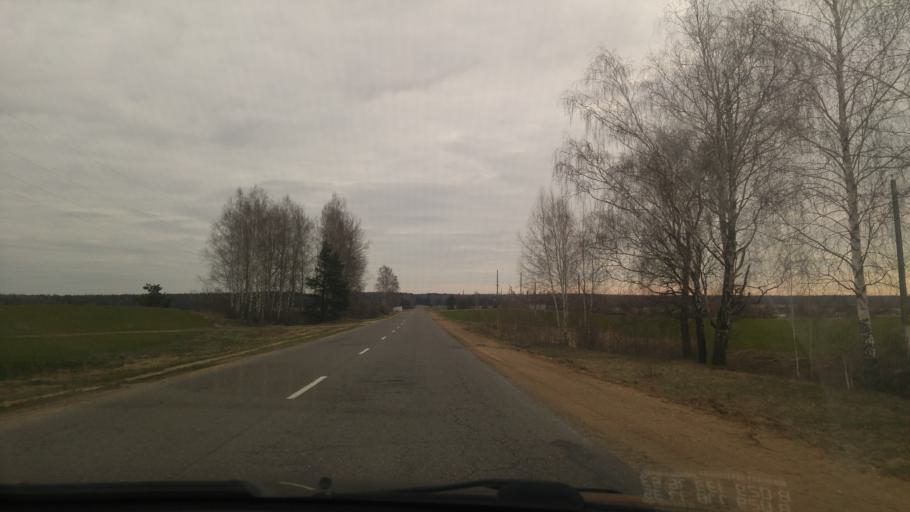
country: BY
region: Minsk
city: Pukhavichy
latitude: 53.7000
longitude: 28.2262
